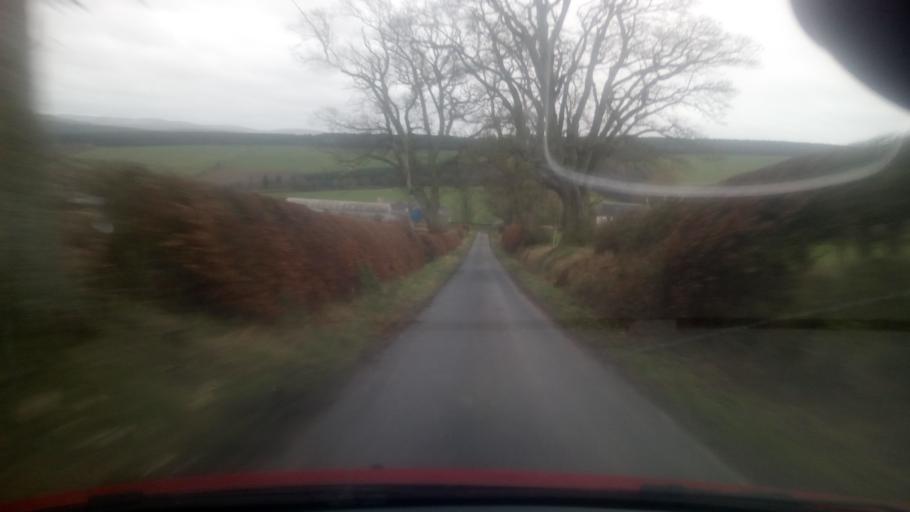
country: GB
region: Scotland
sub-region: The Scottish Borders
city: Jedburgh
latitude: 55.4608
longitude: -2.5149
